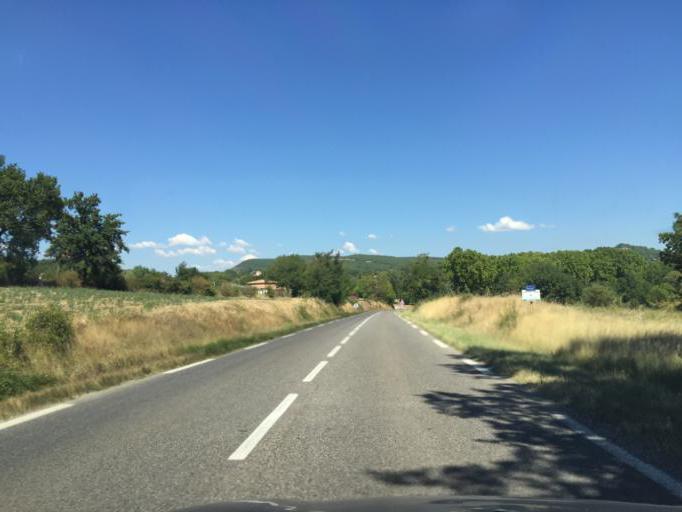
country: FR
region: Provence-Alpes-Cote d'Azur
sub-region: Departement des Alpes-de-Haute-Provence
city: Mane
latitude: 43.9264
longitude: 5.7574
